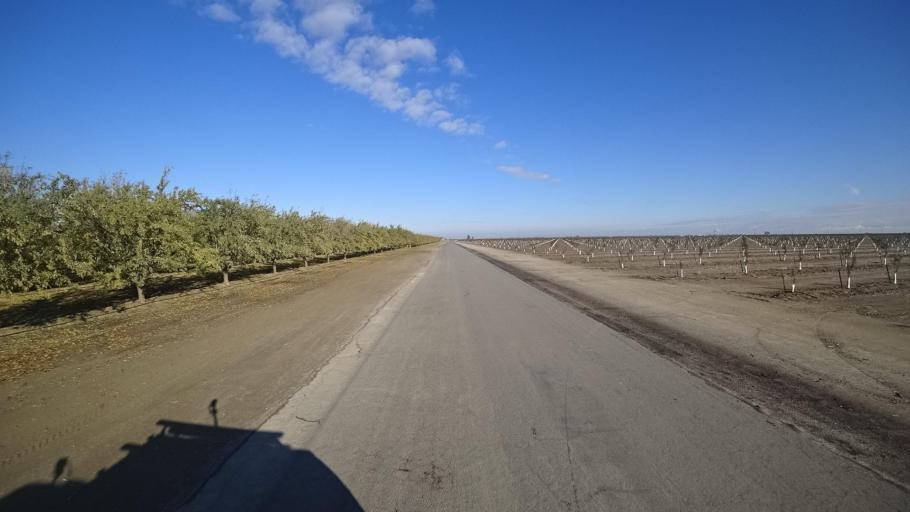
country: US
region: California
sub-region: Kern County
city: McFarland
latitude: 35.7061
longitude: -119.2941
